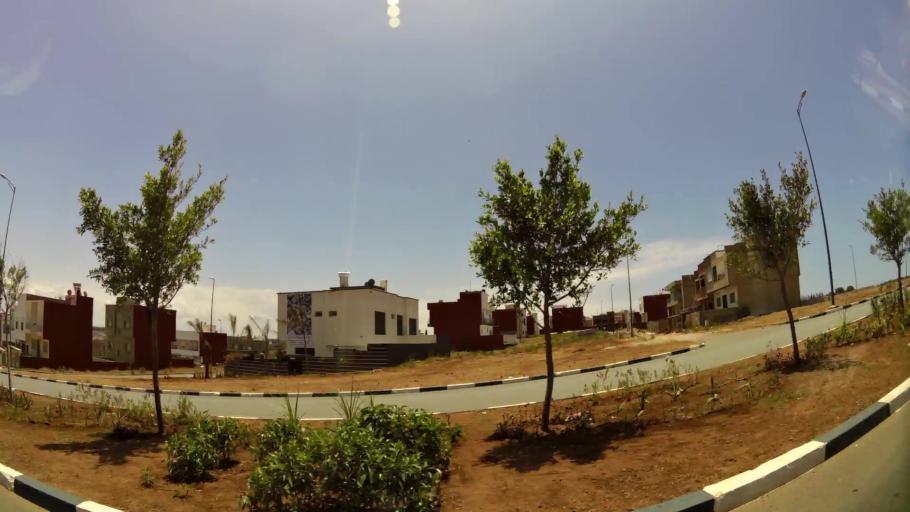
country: MA
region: Gharb-Chrarda-Beni Hssen
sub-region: Kenitra Province
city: Kenitra
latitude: 34.2574
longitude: -6.6547
